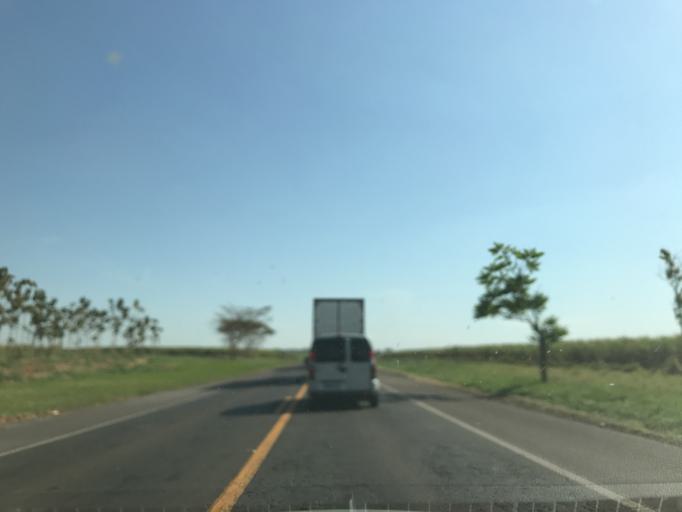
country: BR
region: Sao Paulo
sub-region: Penapolis
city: Penapolis
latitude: -21.4802
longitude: -50.2027
